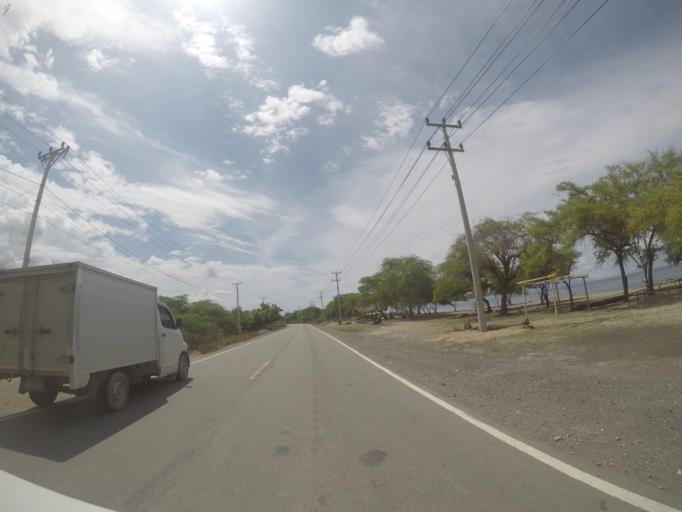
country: TL
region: Liquica
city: Liquica
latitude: -8.5649
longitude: 125.3951
